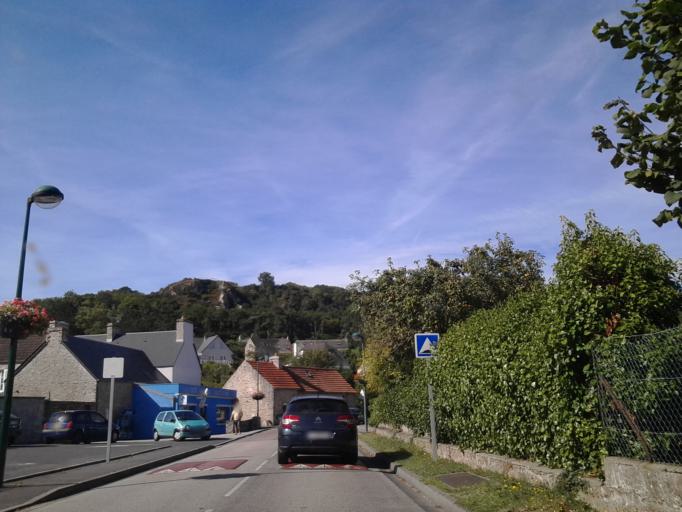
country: FR
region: Lower Normandy
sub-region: Departement de la Manche
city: Bretteville
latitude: 49.6543
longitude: -1.5304
